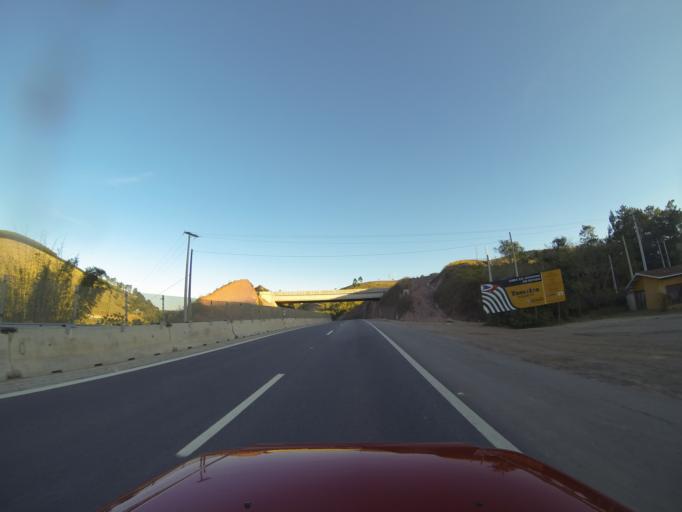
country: BR
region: Sao Paulo
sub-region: Santa Branca
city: Santa Branca
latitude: -23.4039
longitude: -45.6503
